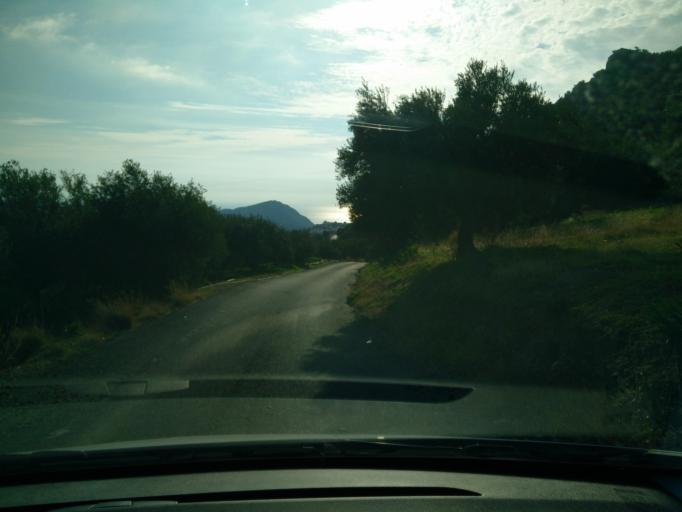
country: GR
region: Crete
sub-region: Nomos Lasithiou
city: Gra Liyia
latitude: 35.0254
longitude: 25.5612
